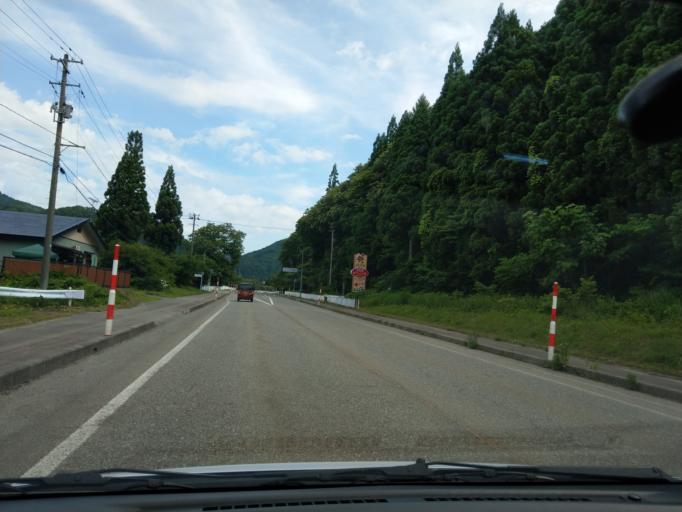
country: JP
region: Akita
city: Kakunodatemachi
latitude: 39.6878
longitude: 140.5553
